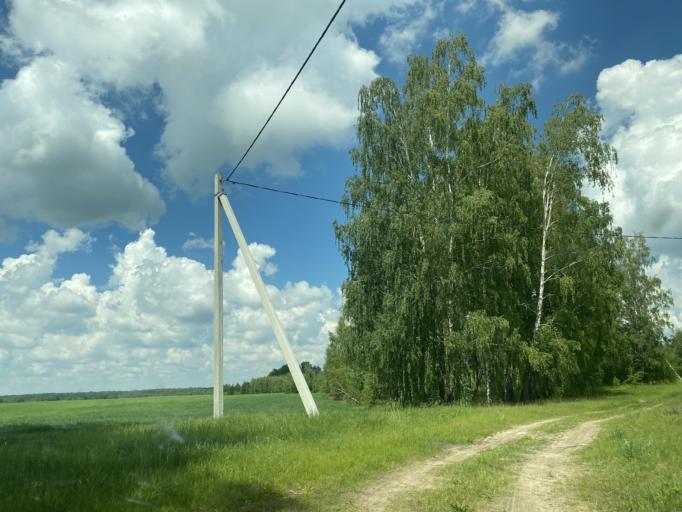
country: BY
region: Brest
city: Ivanava
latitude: 52.2008
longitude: 25.6133
